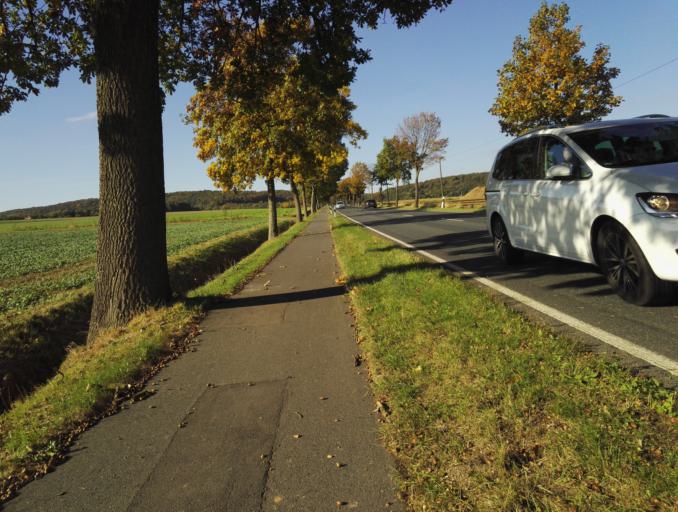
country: DE
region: Lower Saxony
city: Holle
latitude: 52.1143
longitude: 10.1043
